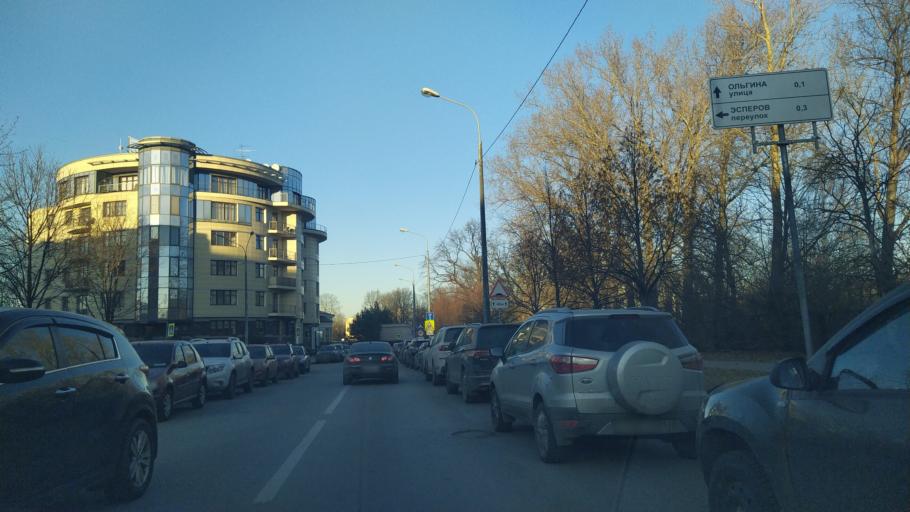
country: RU
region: St.-Petersburg
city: Novaya Derevnya
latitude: 59.9729
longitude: 30.2761
